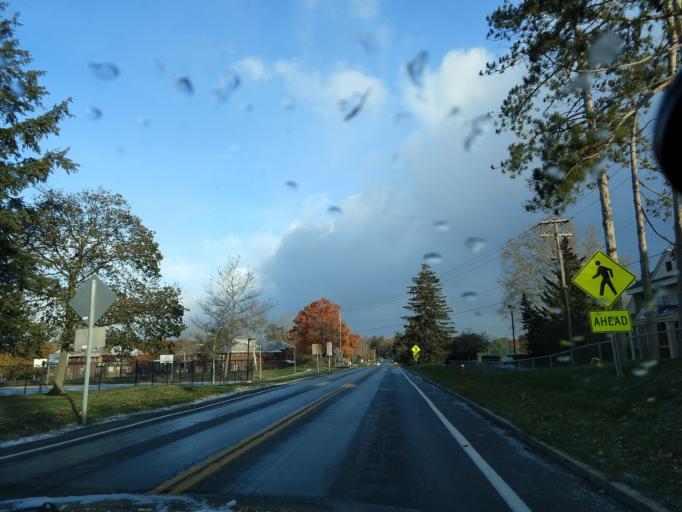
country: US
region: New York
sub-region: Tompkins County
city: Cayuga Heights
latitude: 42.4561
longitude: -76.4738
